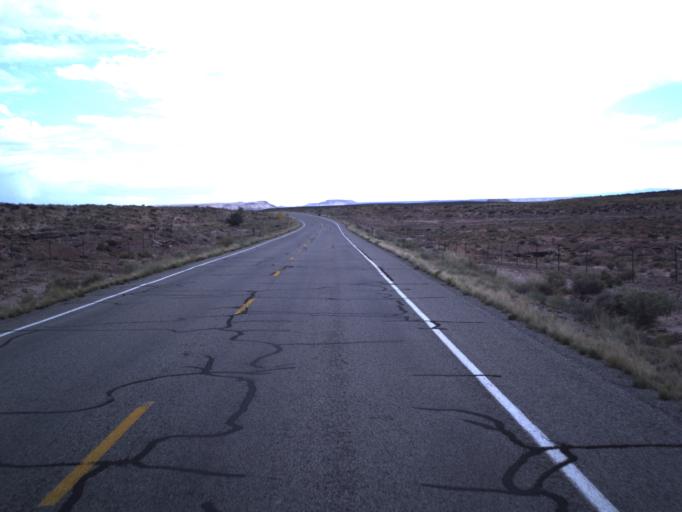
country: US
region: Utah
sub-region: San Juan County
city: Blanding
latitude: 37.2973
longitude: -109.4280
